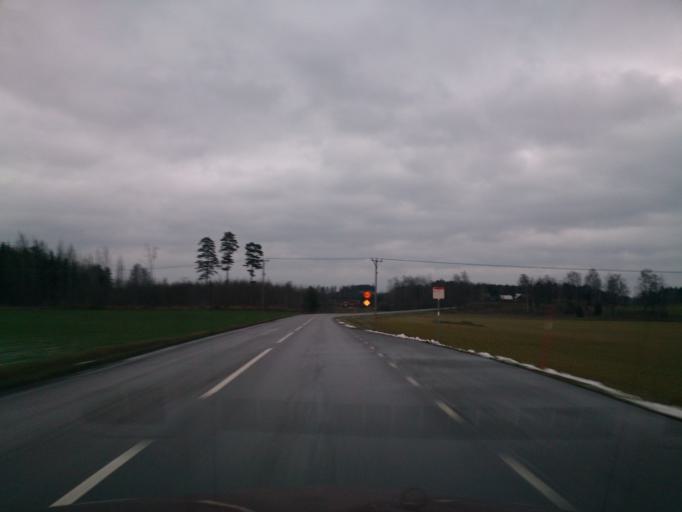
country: SE
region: OEstergoetland
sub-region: Linkopings Kommun
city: Linghem
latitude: 58.4104
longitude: 15.8750
